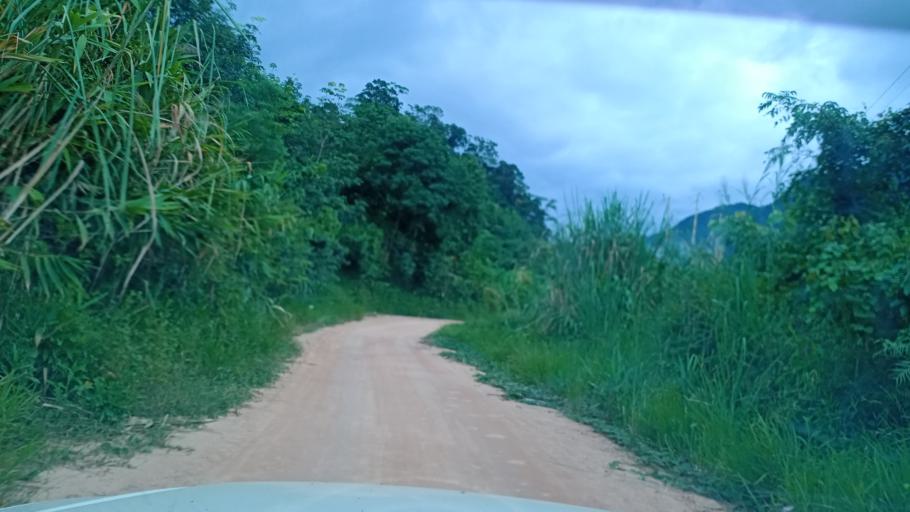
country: TH
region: Changwat Bueng Kan
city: Pak Khat
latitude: 18.7267
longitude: 103.2767
